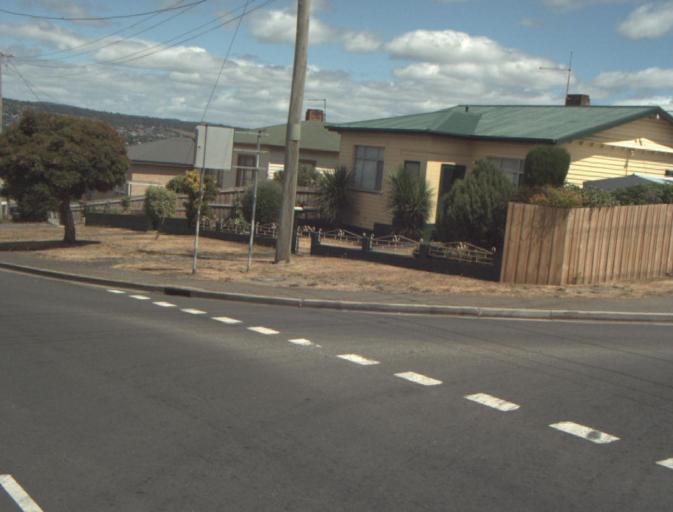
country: AU
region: Tasmania
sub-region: Launceston
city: Newstead
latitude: -41.4216
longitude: 147.1680
